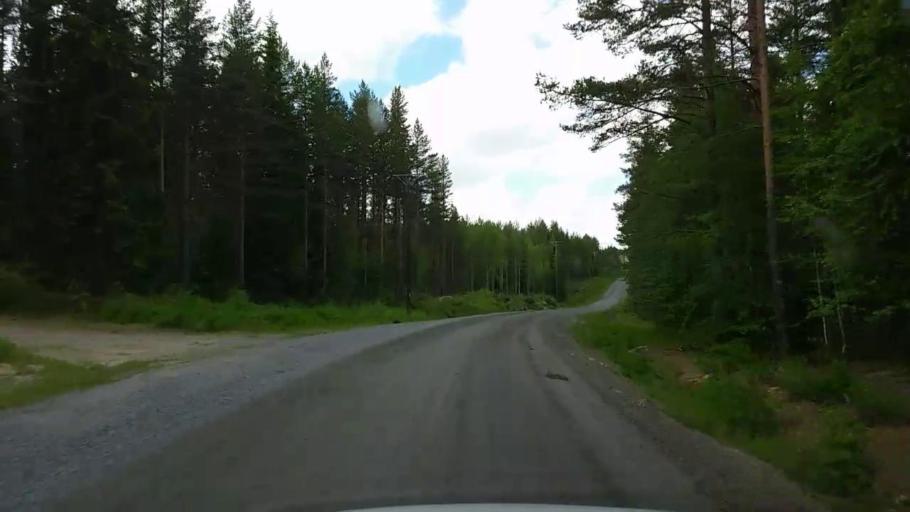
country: SE
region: Gaevleborg
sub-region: Bollnas Kommun
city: Vittsjo
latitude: 61.0687
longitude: 16.2822
